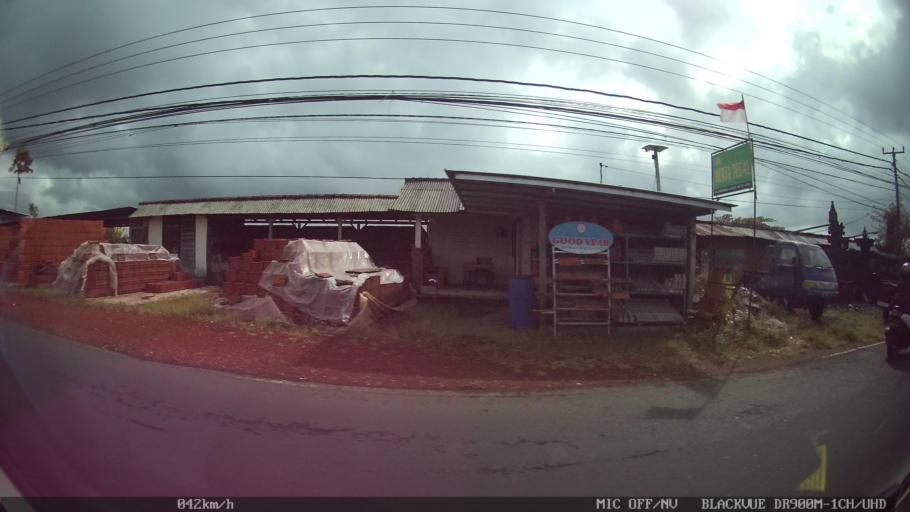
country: ID
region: Bali
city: Banjar Bucu
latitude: -8.5869
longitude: 115.2025
